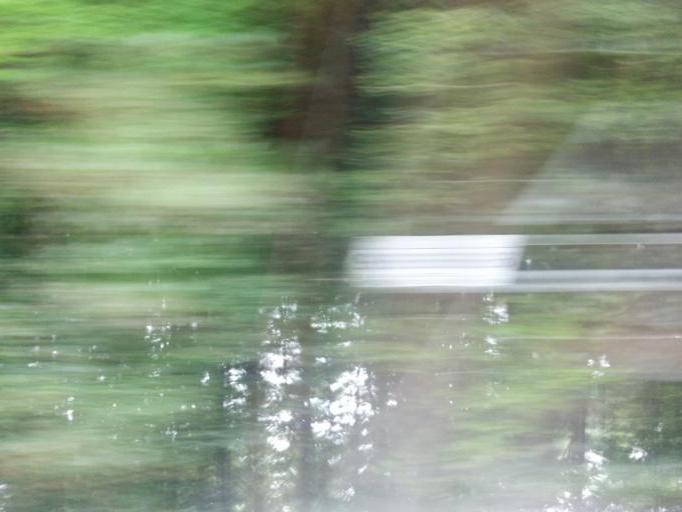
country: JP
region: Tochigi
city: Kanuma
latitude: 36.6206
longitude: 139.7349
